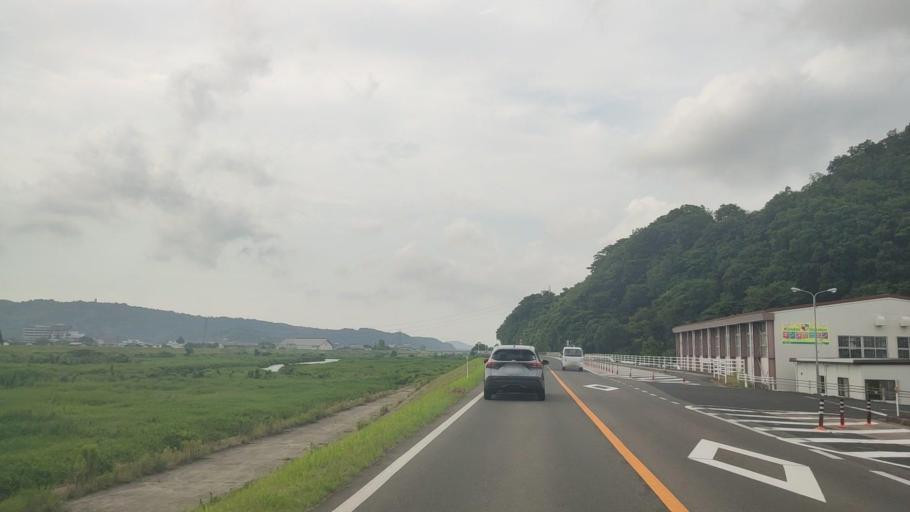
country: JP
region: Tottori
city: Kurayoshi
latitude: 35.4290
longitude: 133.8499
